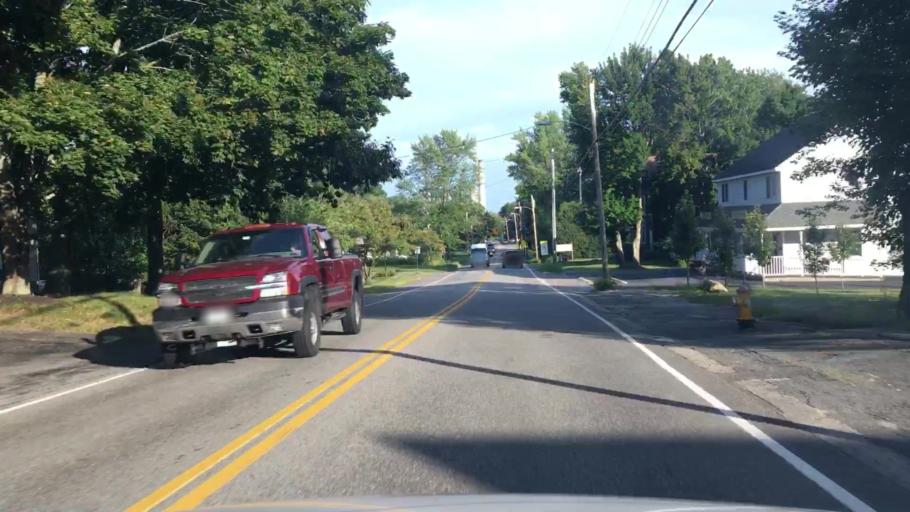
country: US
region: Maine
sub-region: Cumberland County
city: Westbrook
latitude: 43.6904
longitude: -70.3646
